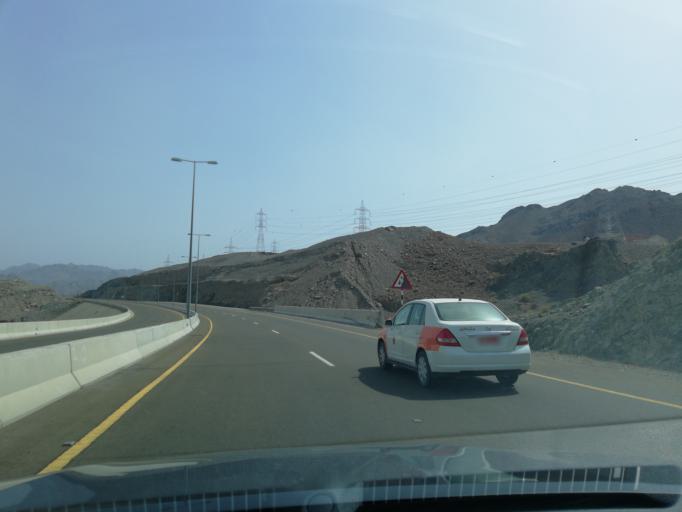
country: OM
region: Al Batinah
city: Al Liwa'
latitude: 24.2522
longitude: 56.3549
